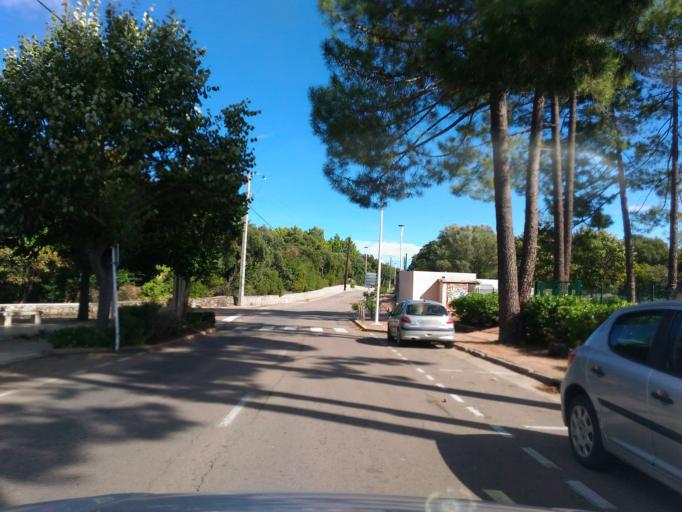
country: FR
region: Corsica
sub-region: Departement de la Corse-du-Sud
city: Porto-Vecchio
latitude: 41.6992
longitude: 9.3497
